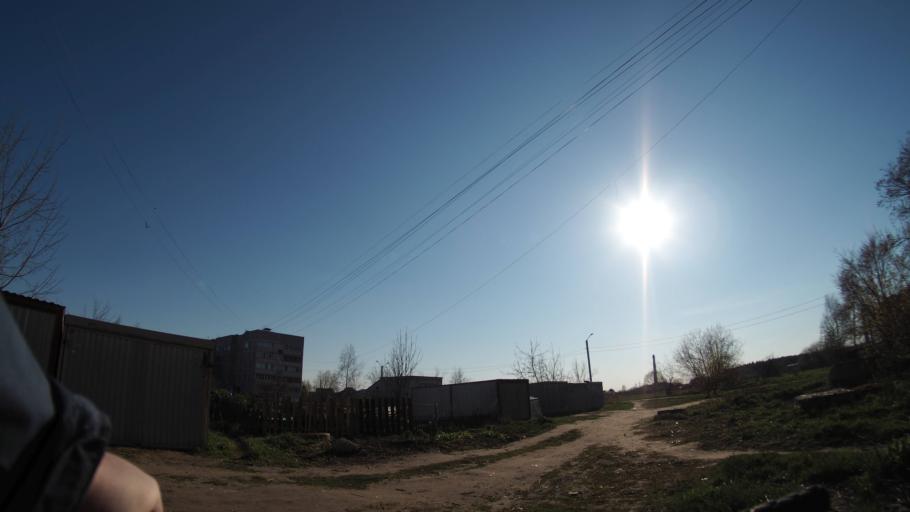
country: RU
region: Moskovskaya
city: Malyshevo
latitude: 55.5058
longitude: 38.3382
